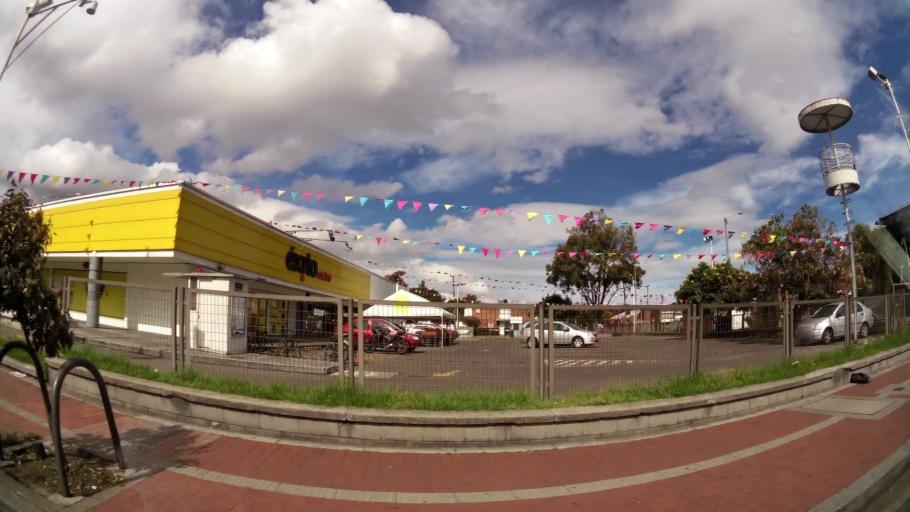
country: CO
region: Bogota D.C.
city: Barrio San Luis
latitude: 4.7058
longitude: -74.0712
